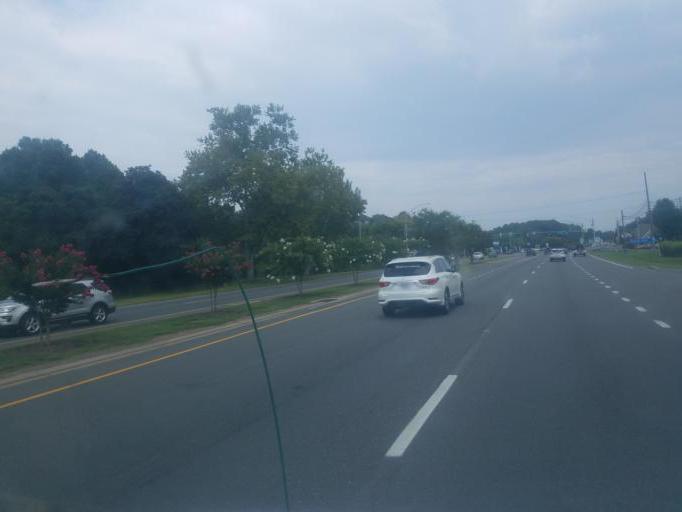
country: US
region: Maryland
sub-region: Worcester County
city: West Ocean City
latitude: 38.3391
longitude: -75.1282
